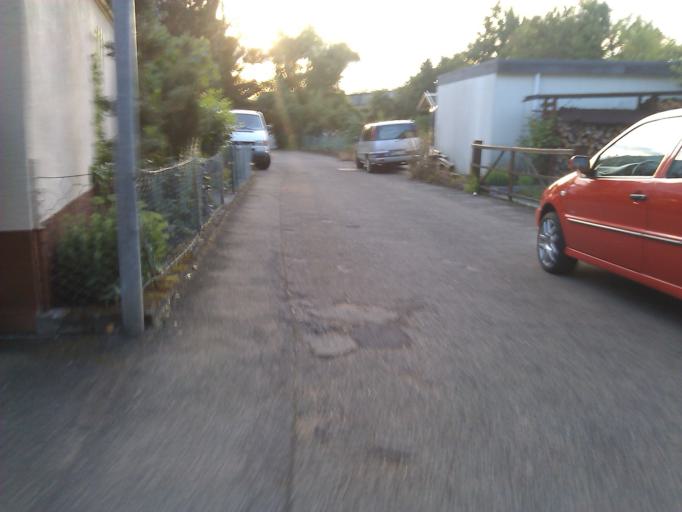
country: DE
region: Baden-Wuerttemberg
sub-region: Regierungsbezirk Stuttgart
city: Untereisesheim
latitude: 49.2361
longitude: 9.1911
